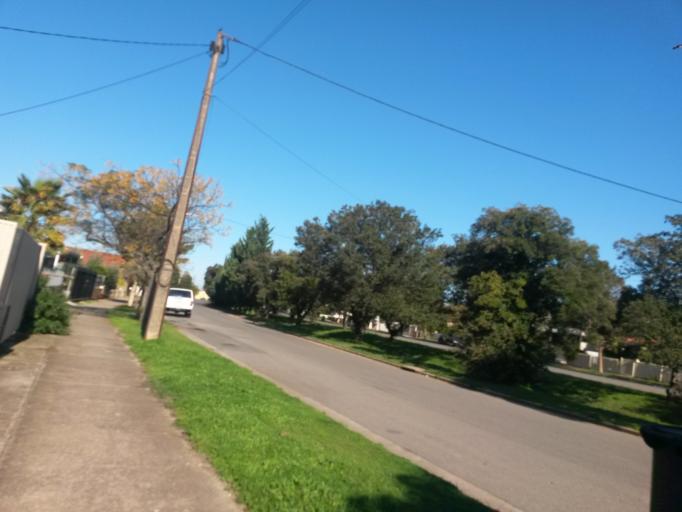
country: AU
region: South Australia
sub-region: Port Adelaide Enfield
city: Alberton
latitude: -34.8491
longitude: 138.5250
